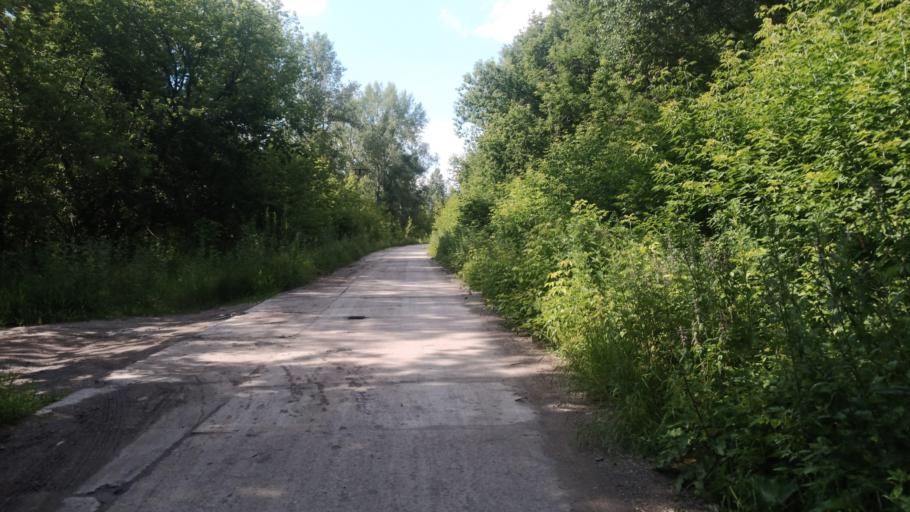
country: RU
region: Altai Krai
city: Zaton
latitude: 53.3376
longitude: 83.8068
